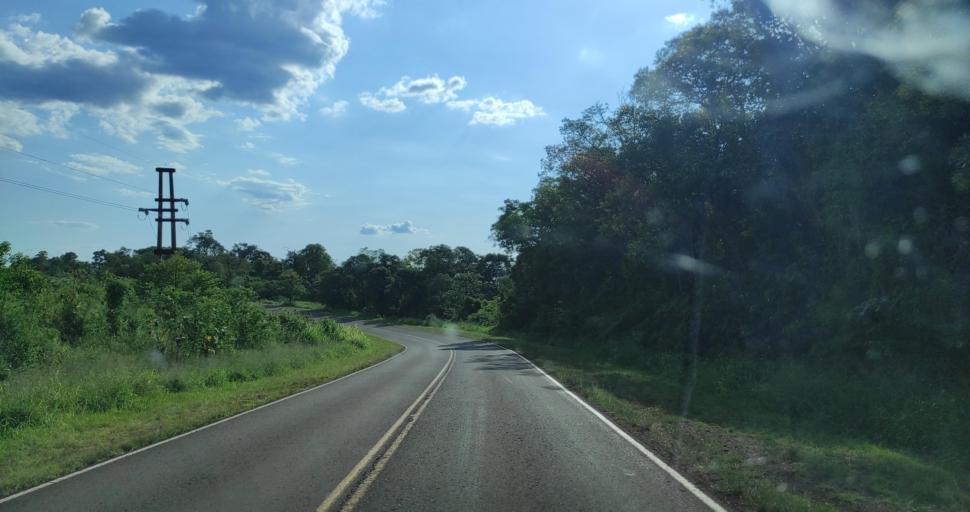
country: AR
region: Misiones
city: San Vicente
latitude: -26.3507
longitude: -54.2082
